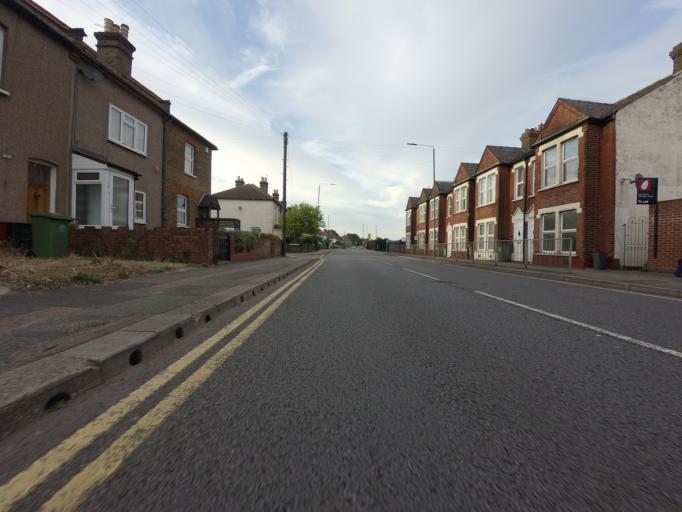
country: GB
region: England
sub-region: Greater London
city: Sidcup
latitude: 51.4152
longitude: 0.1143
